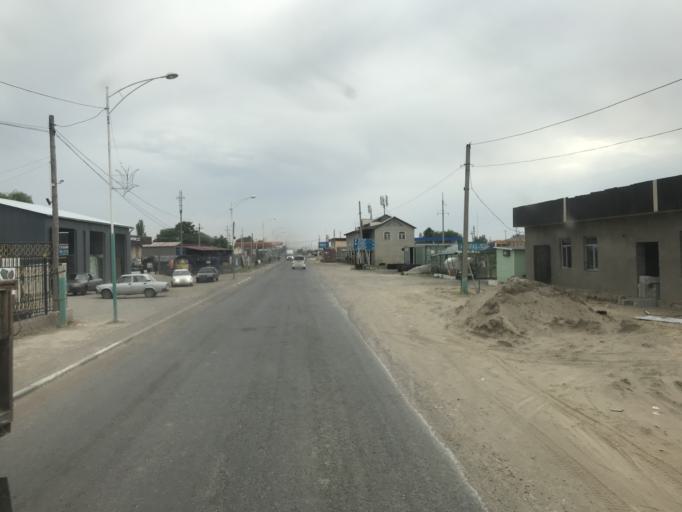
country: KZ
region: Ongtustik Qazaqstan
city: Asykata
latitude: 40.9024
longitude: 68.3612
